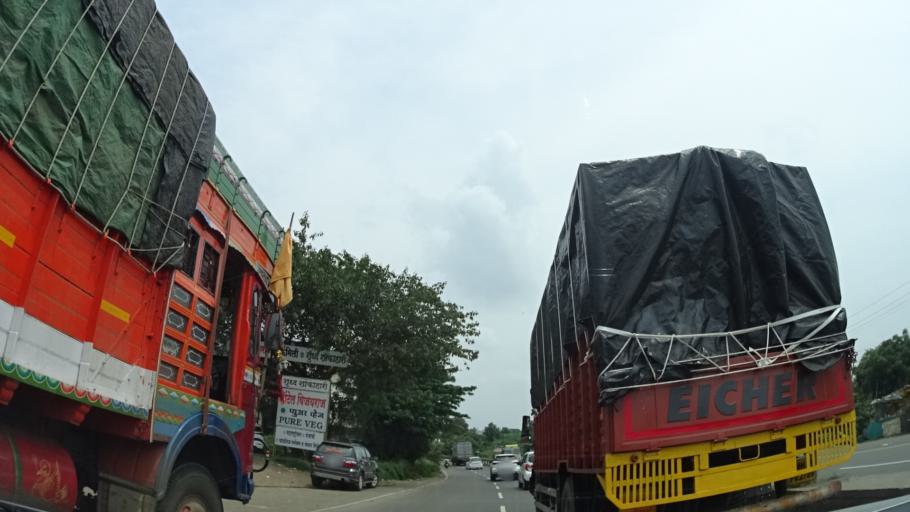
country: IN
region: Maharashtra
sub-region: Pune Division
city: Koregaon
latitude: 18.7251
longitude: 74.1989
